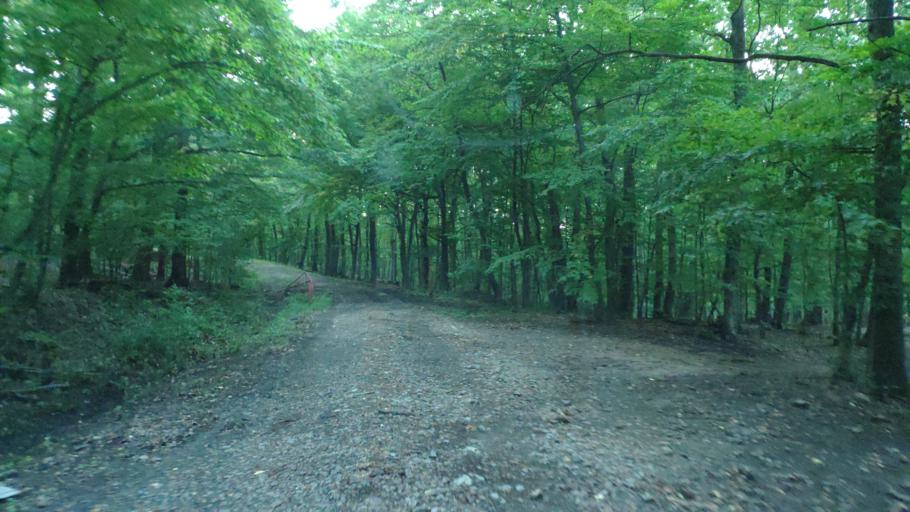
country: SK
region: Kosicky
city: Secovce
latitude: 48.5831
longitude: 21.5340
